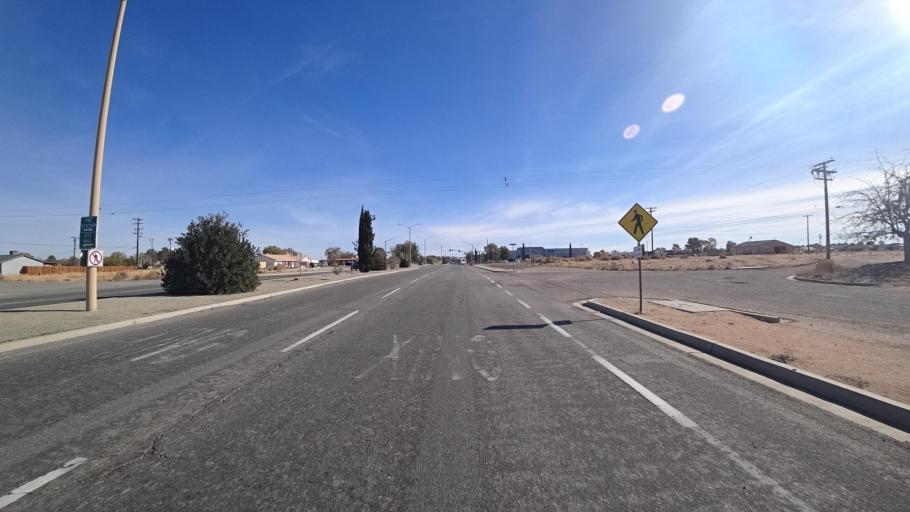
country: US
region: California
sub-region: Kern County
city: California City
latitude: 35.1257
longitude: -117.9614
